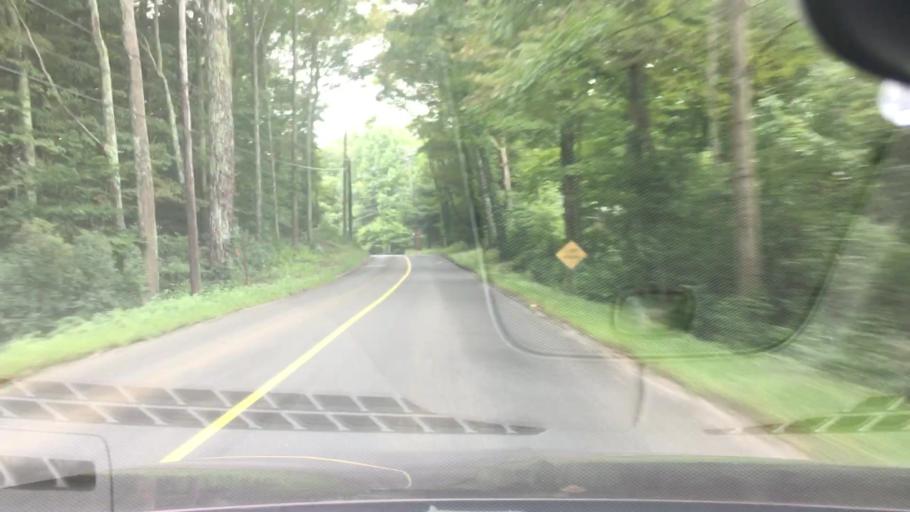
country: US
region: Connecticut
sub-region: New Haven County
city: Madison
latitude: 41.3401
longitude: -72.5736
